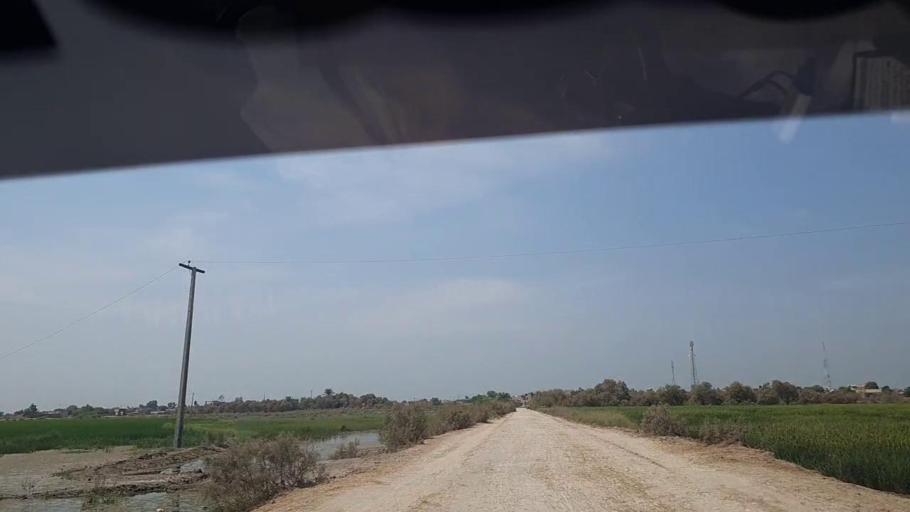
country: PK
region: Sindh
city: Thul
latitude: 28.1770
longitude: 68.7337
